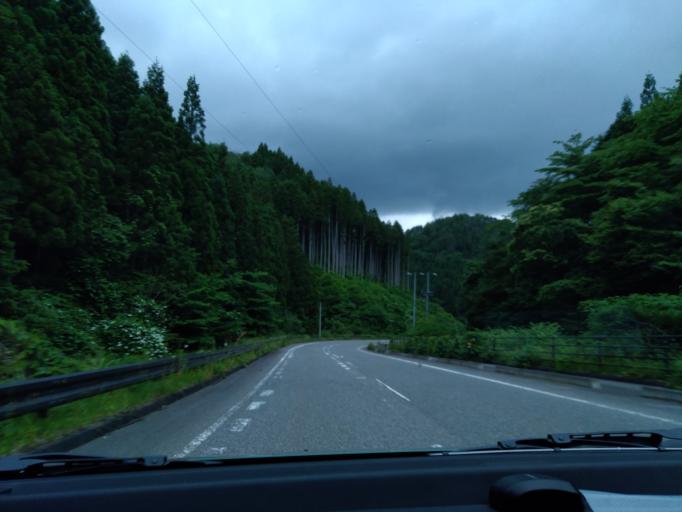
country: JP
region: Iwate
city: Ichinoseki
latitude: 38.8182
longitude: 140.9022
